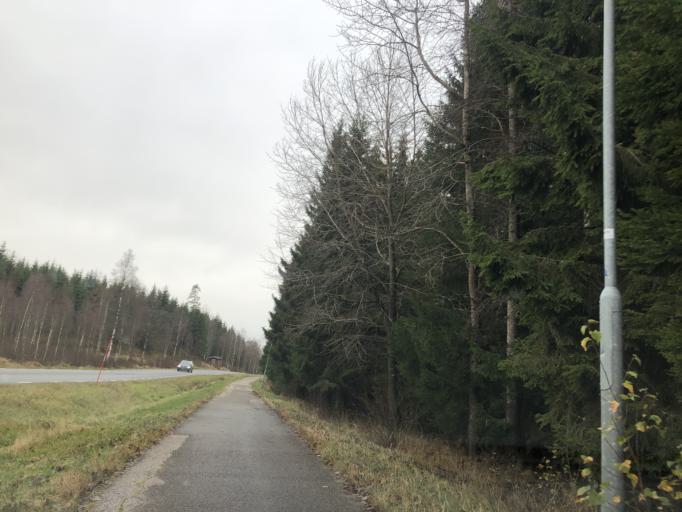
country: SE
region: Vaestra Goetaland
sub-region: Ulricehamns Kommun
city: Ulricehamn
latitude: 57.6741
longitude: 13.4504
